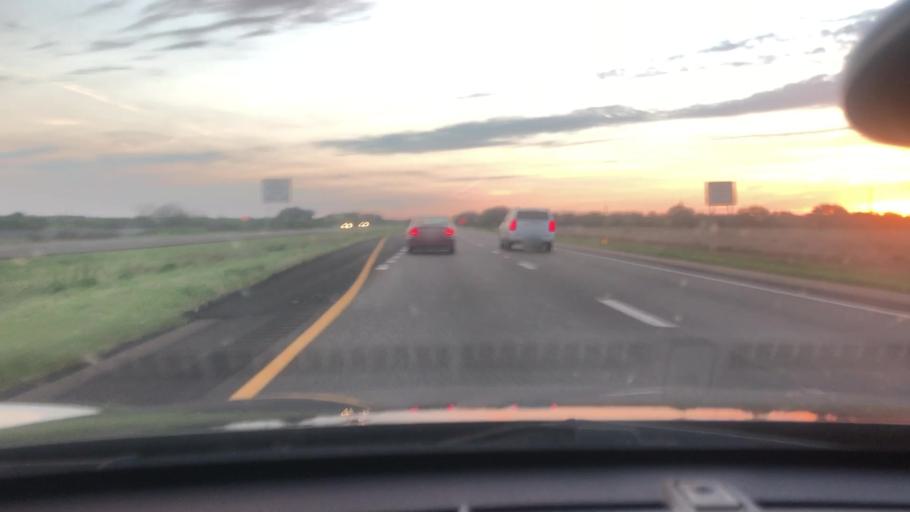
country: US
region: Texas
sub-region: Victoria County
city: Inez
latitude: 28.9216
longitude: -96.7580
